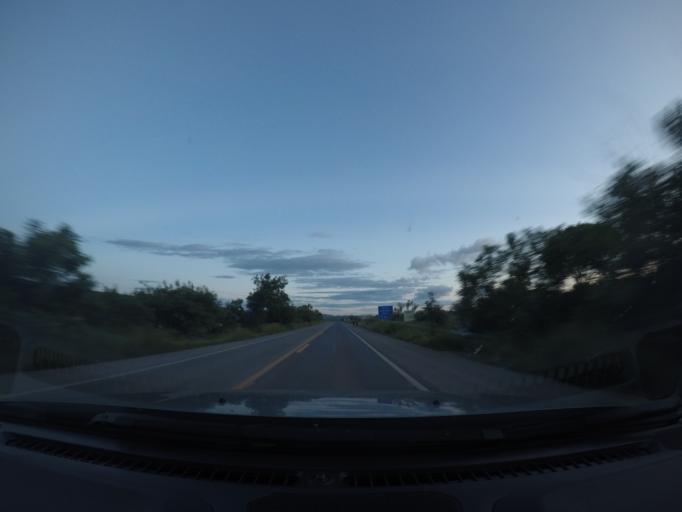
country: BR
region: Bahia
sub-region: Seabra
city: Seabra
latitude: -12.4620
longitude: -41.7471
